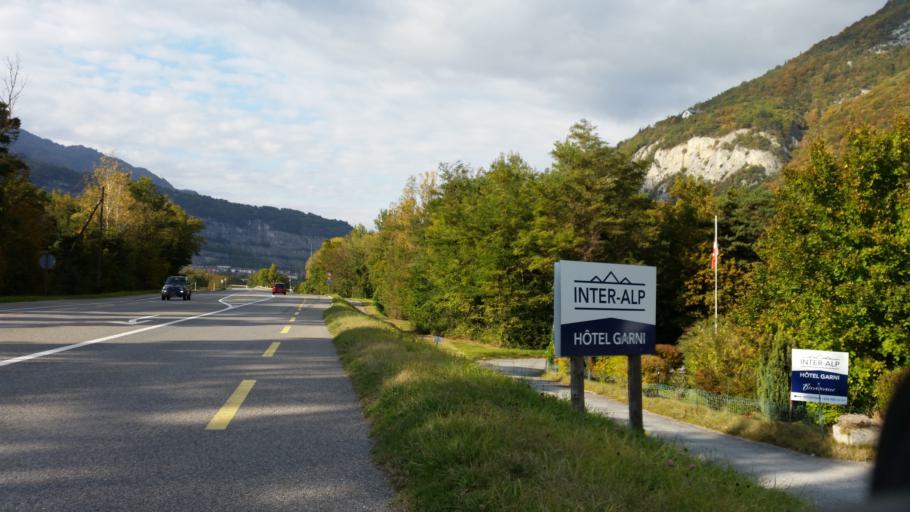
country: CH
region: Valais
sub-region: Martigny District
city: Evionnaz
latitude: 46.1966
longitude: 7.0212
